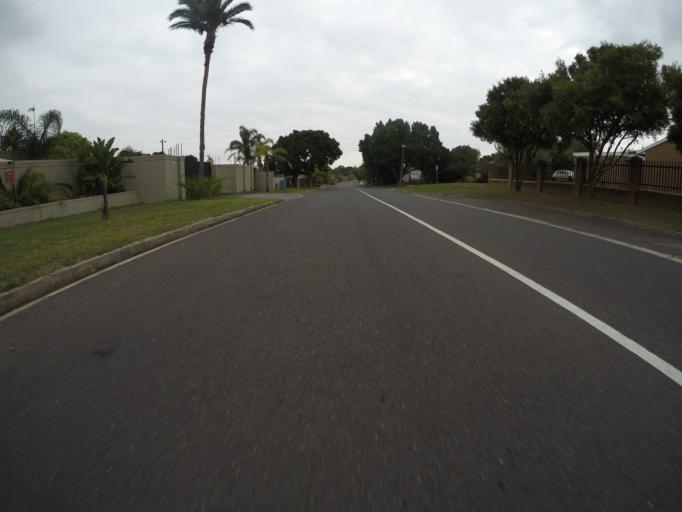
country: ZA
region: Western Cape
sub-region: City of Cape Town
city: Kraaifontein
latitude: -33.8687
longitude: 18.6489
